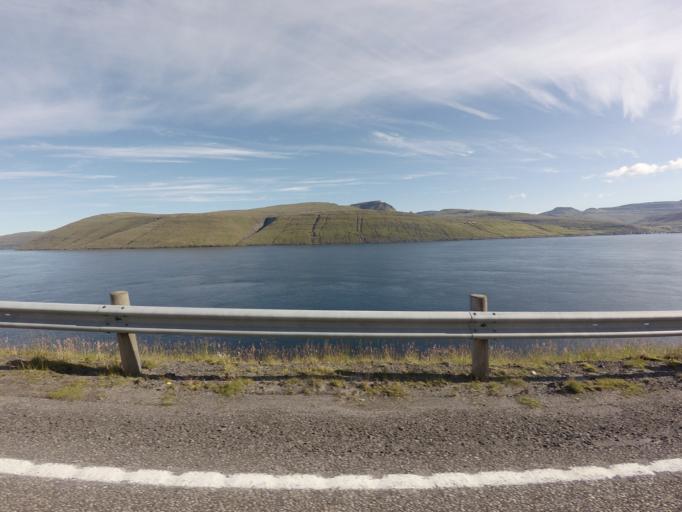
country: FO
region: Streymoy
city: Vestmanna
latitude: 62.1000
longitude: -7.1218
